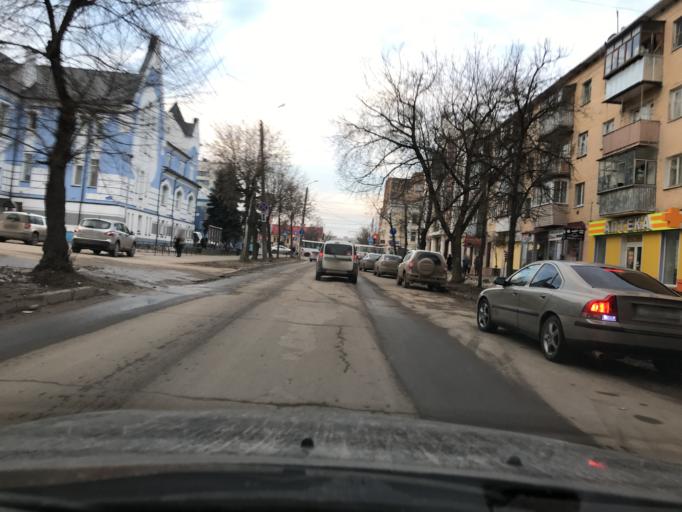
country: RU
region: Kaluga
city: Kaluga
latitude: 54.5144
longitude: 36.2472
